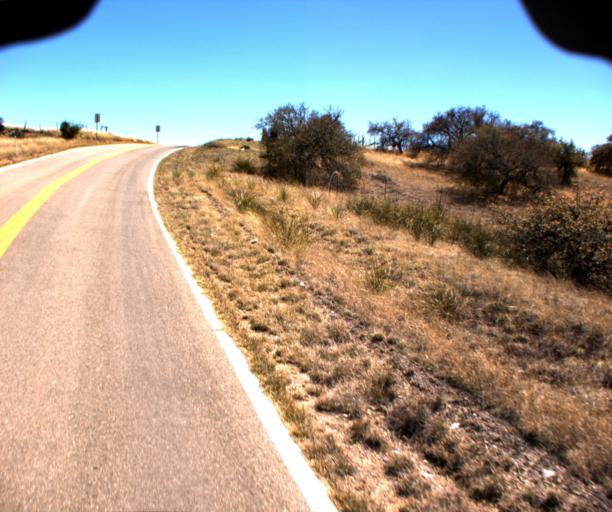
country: US
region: Arizona
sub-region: Cochise County
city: Huachuca City
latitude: 31.6047
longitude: -110.5788
